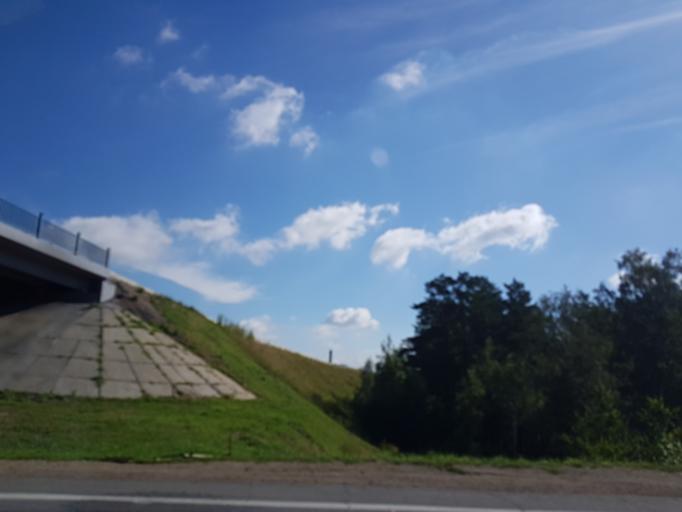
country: RU
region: Irkutsk
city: Meget
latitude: 52.3605
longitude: 104.1279
